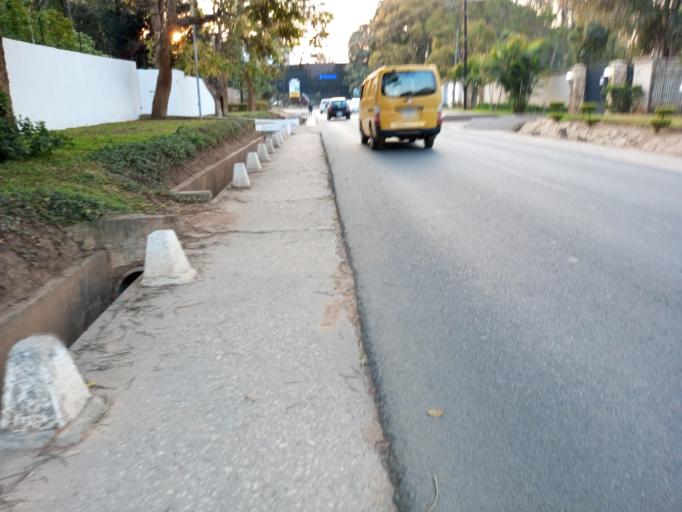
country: ZM
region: Lusaka
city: Lusaka
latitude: -15.4089
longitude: 28.3015
